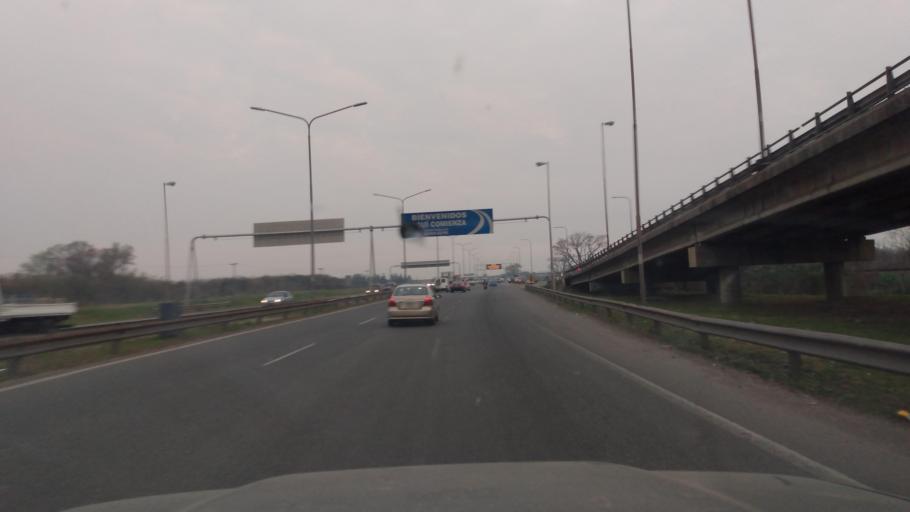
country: AR
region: Buenos Aires
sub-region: Partido de Tigre
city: Tigre
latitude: -34.4891
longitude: -58.5966
